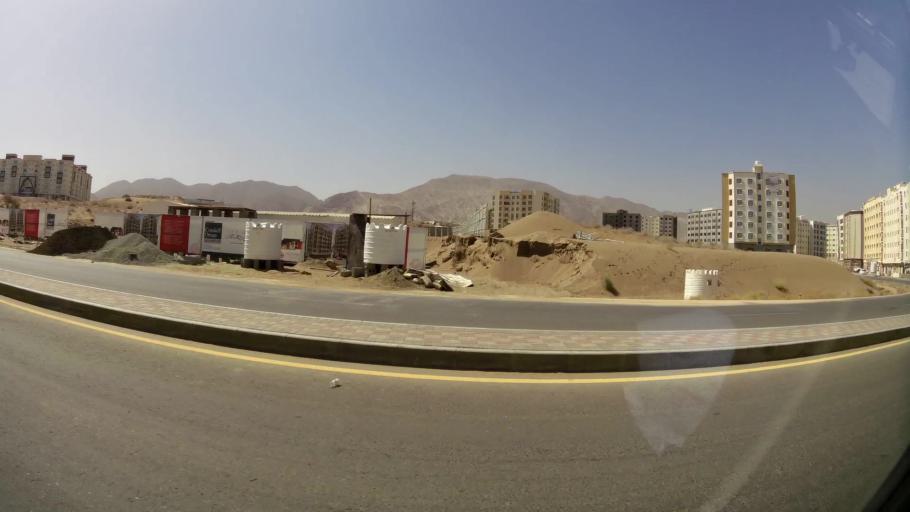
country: OM
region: Muhafazat Masqat
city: Bawshar
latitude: 23.5745
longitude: 58.4103
